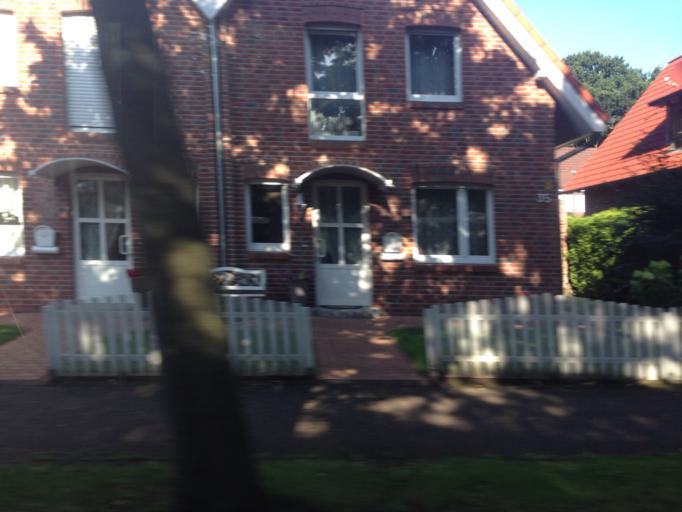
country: DE
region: North Rhine-Westphalia
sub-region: Regierungsbezirk Munster
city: Senden
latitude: 51.8613
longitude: 7.4812
